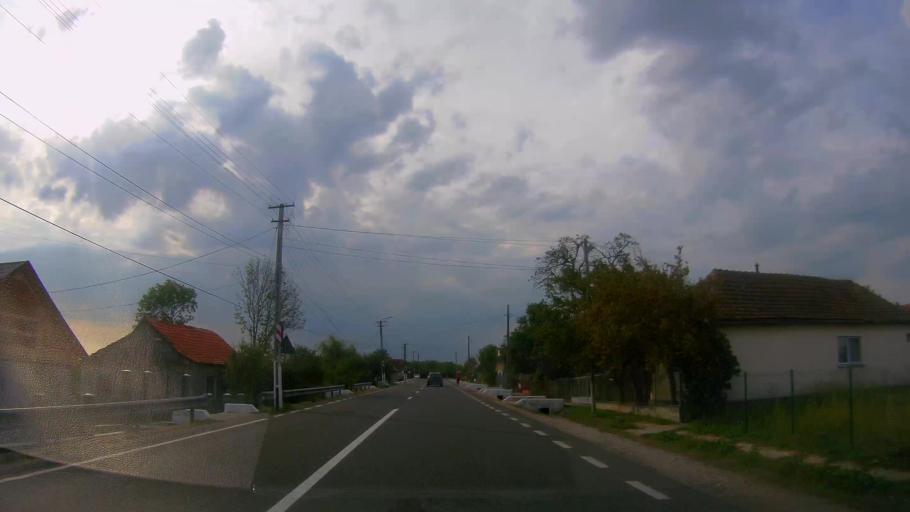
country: RO
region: Satu Mare
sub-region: Oras Ardud
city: Ardud
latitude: 47.5941
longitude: 22.8800
